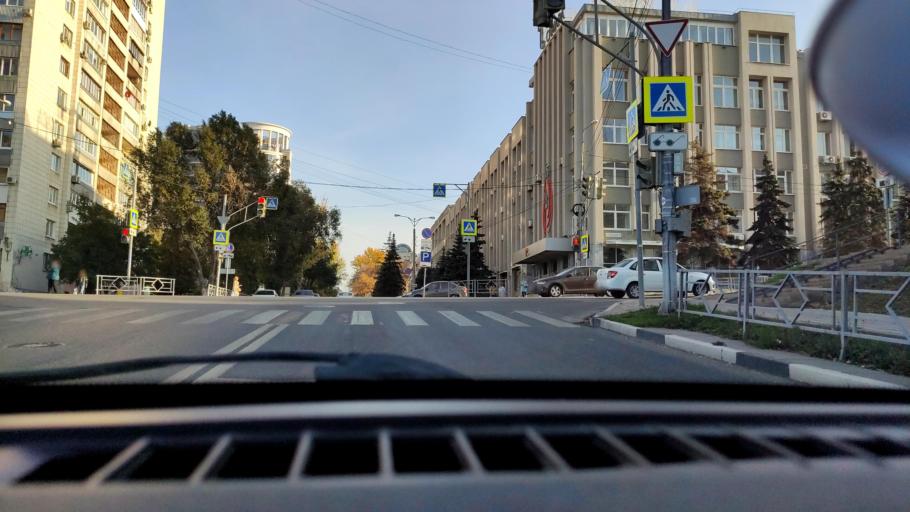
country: RU
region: Samara
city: Samara
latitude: 53.2042
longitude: 50.1140
